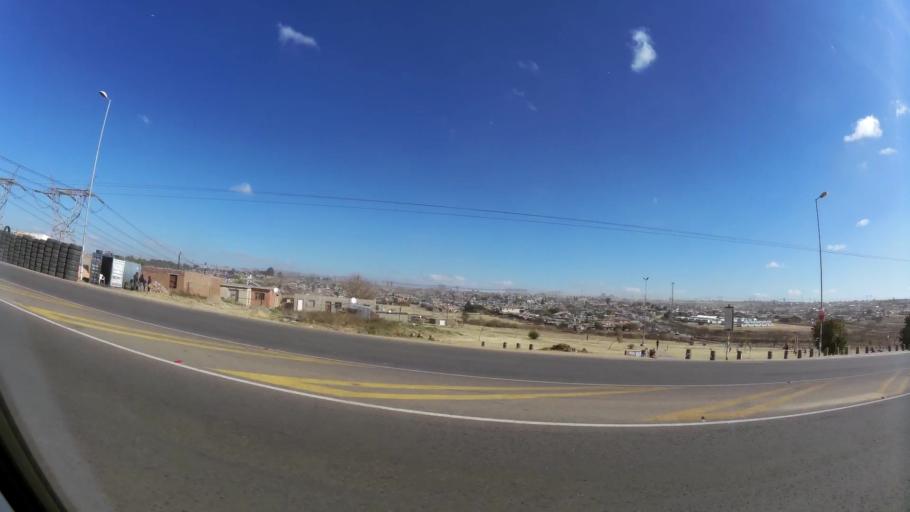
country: ZA
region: Gauteng
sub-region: City of Johannesburg Metropolitan Municipality
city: Midrand
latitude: -25.9193
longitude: 28.0995
